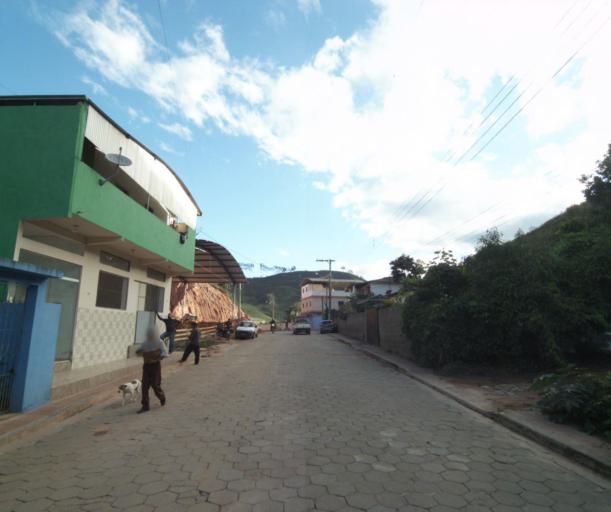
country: BR
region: Espirito Santo
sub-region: Guacui
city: Guacui
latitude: -20.6241
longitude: -41.6876
